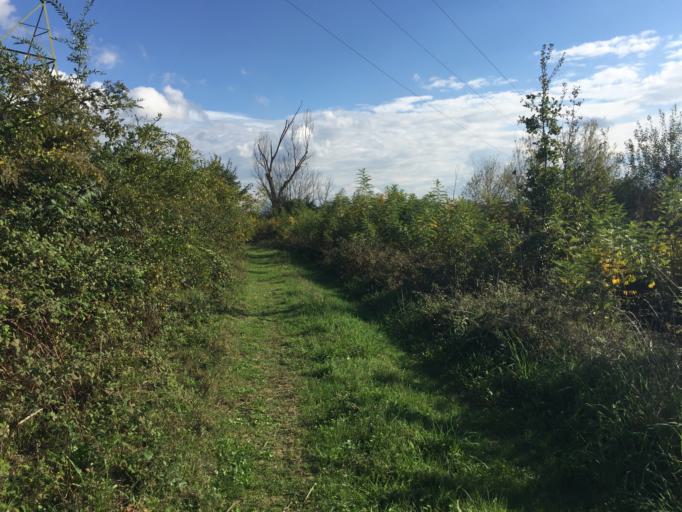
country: IT
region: Tuscany
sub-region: Provincia di Lucca
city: Spianate
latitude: 43.8282
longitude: 10.6982
